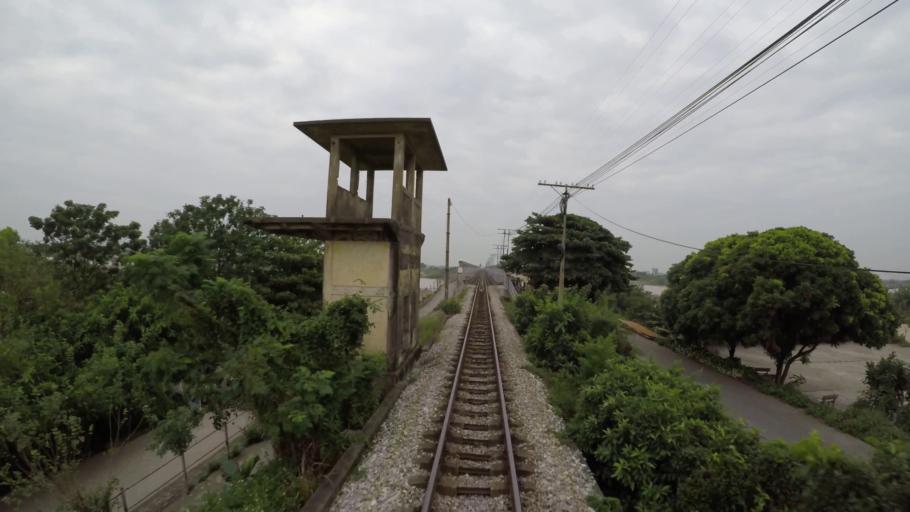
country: VN
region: Hai Duong
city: Thanh Pho Hai Duong
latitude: 20.9541
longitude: 106.3632
